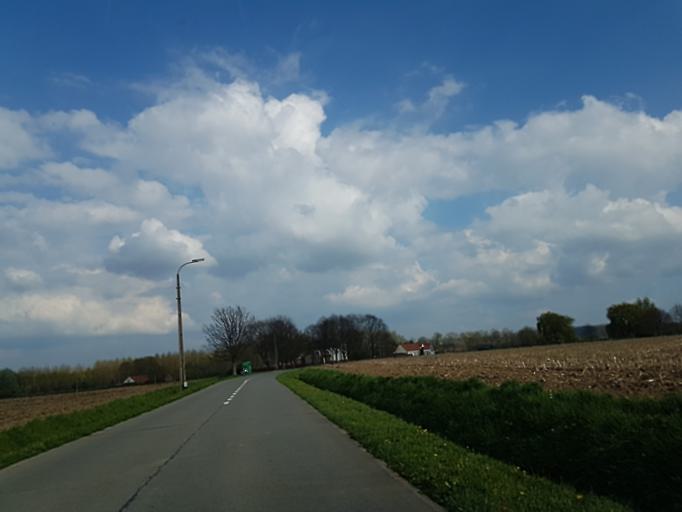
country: BE
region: Flanders
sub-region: Provincie Oost-Vlaanderen
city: Oudenaarde
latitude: 50.8489
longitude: 3.5675
